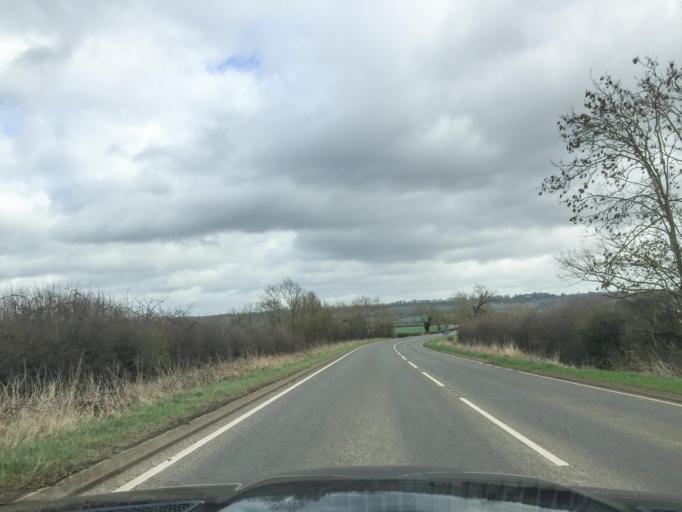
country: GB
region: England
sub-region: Warwickshire
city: Wellesbourne Mountford
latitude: 52.1225
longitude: -1.5163
